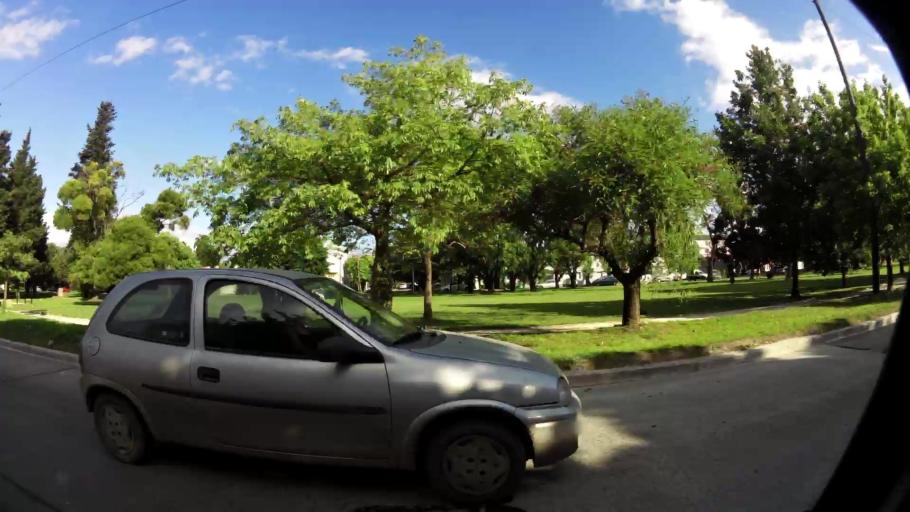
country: AR
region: Buenos Aires
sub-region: Partido de La Plata
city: La Plata
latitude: -34.8909
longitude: -57.9593
